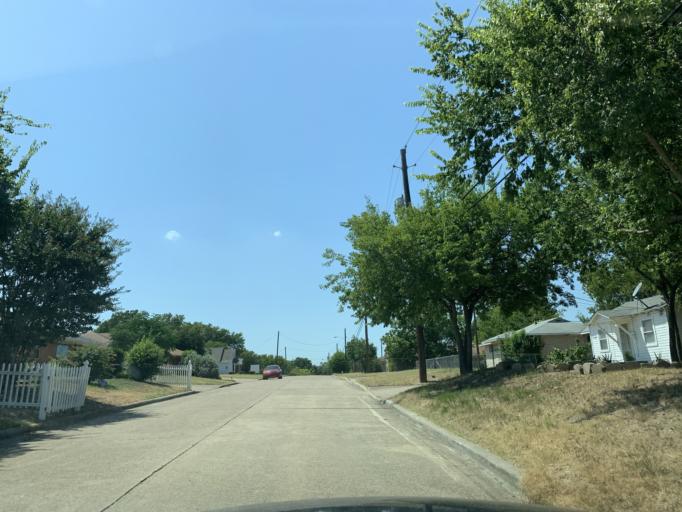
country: US
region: Texas
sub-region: Dallas County
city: Hutchins
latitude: 32.6791
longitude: -96.8067
